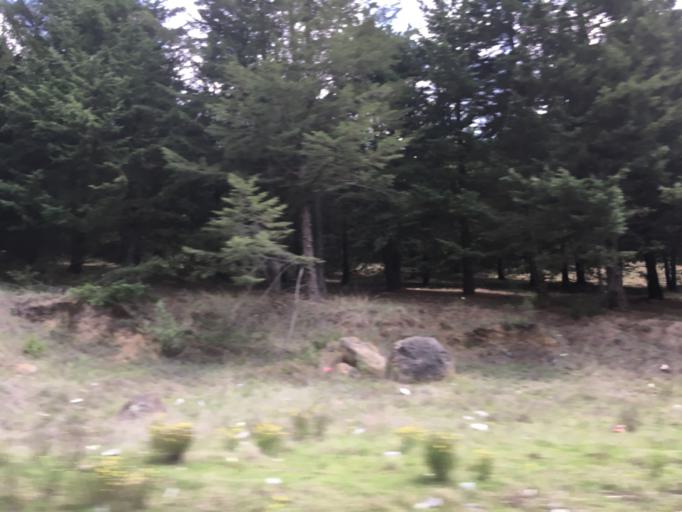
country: MX
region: Mexico
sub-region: Atlacomulco
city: Santiago Acutzilapan
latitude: 19.7851
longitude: -99.7389
